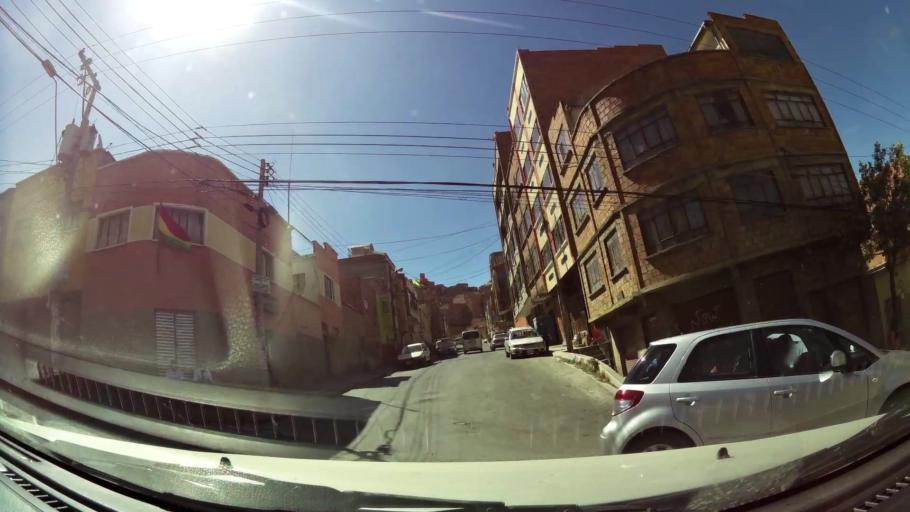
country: BO
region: La Paz
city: La Paz
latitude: -16.4911
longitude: -68.1552
